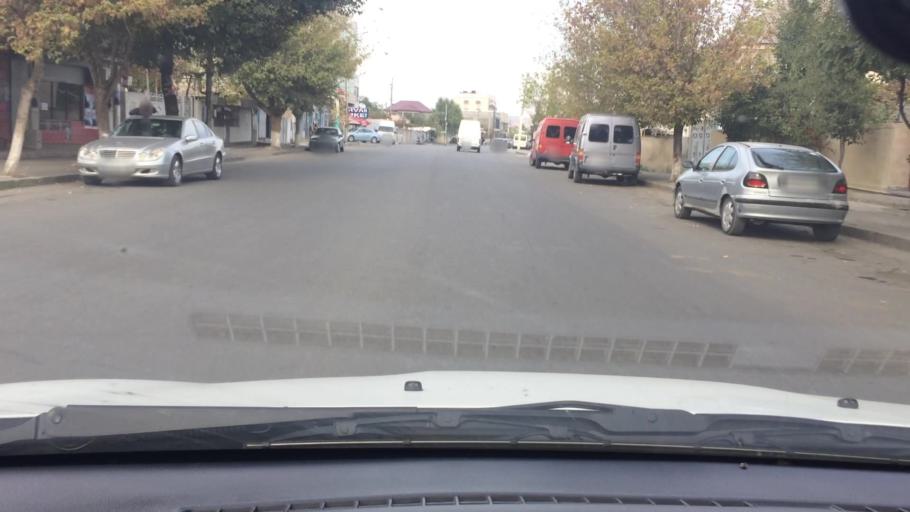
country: GE
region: Kvemo Kartli
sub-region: Marneuli
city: Marneuli
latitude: 41.4649
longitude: 44.8157
